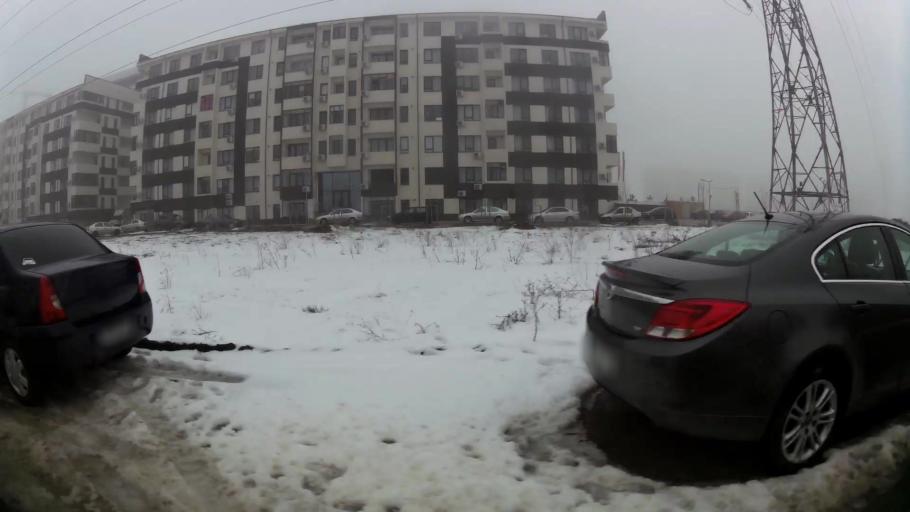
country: RO
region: Ilfov
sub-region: Comuna Chiajna
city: Chiajna
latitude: 44.4413
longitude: 25.9768
